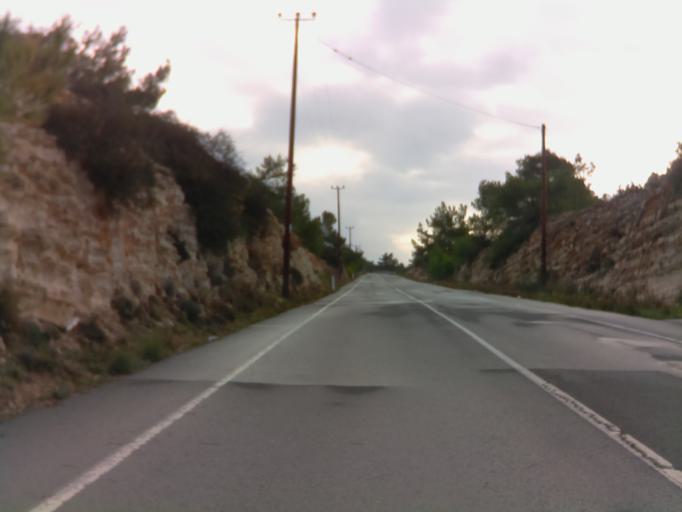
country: CY
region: Pafos
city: Pegeia
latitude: 34.8970
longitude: 32.3746
